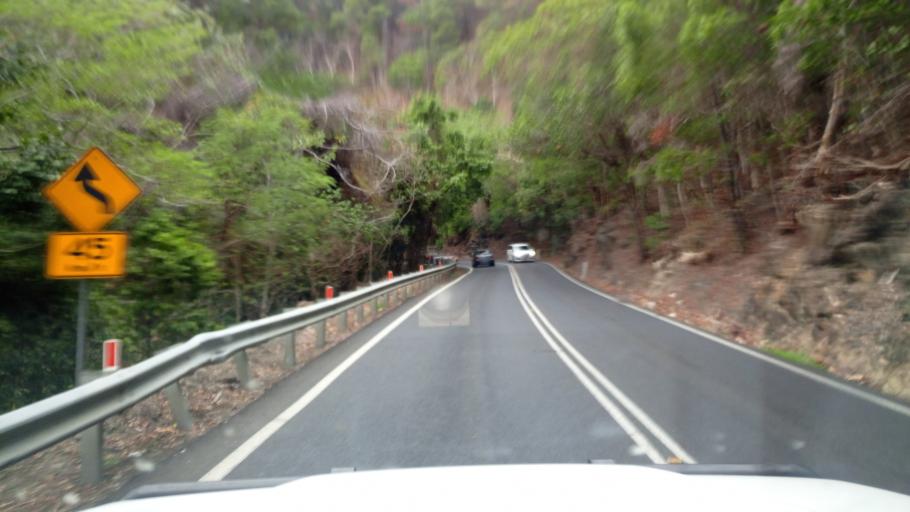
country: AU
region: Queensland
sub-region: Cairns
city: Redlynch
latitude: -16.8474
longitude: 145.6831
